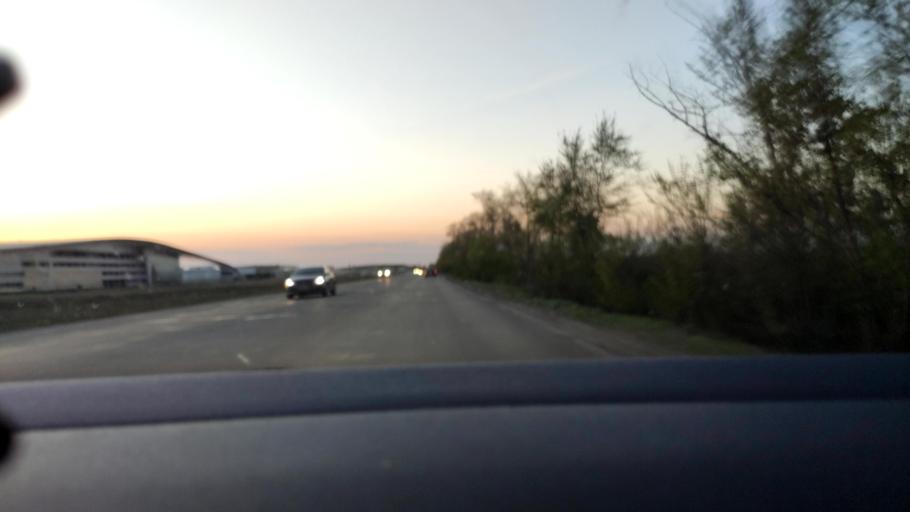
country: RU
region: Voronezj
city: Maslovka
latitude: 51.5380
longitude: 39.2888
